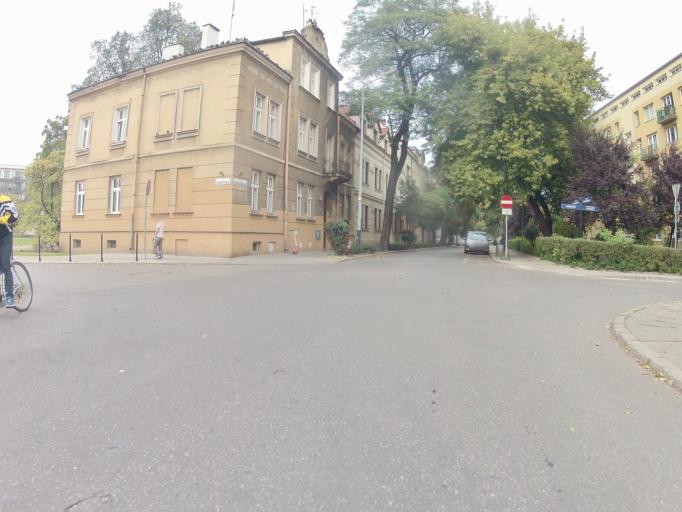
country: PL
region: Lesser Poland Voivodeship
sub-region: Krakow
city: Krakow
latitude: 50.0411
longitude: 19.9401
